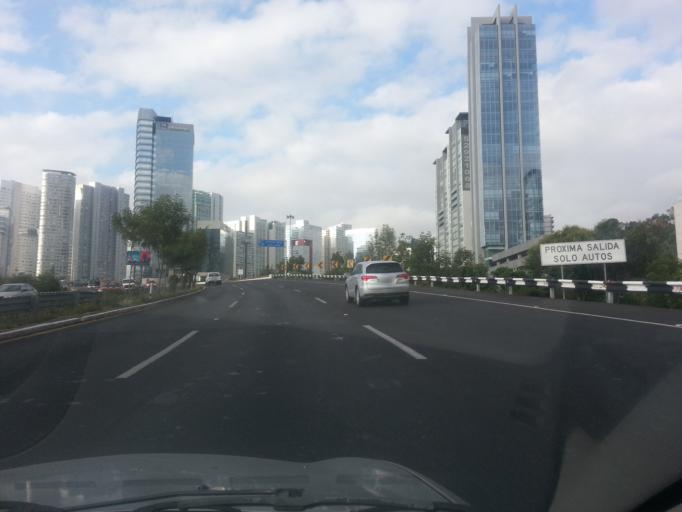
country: MX
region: Mexico City
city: Col. Bosques de las Lomas
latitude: 19.3686
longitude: -99.2666
